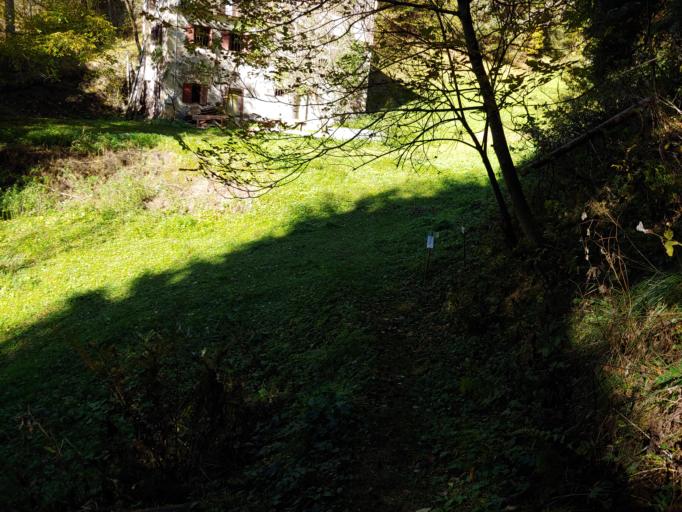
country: IT
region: Veneto
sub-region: Provincia di Belluno
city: Lozzo di Cadore
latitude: 46.4905
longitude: 12.4343
